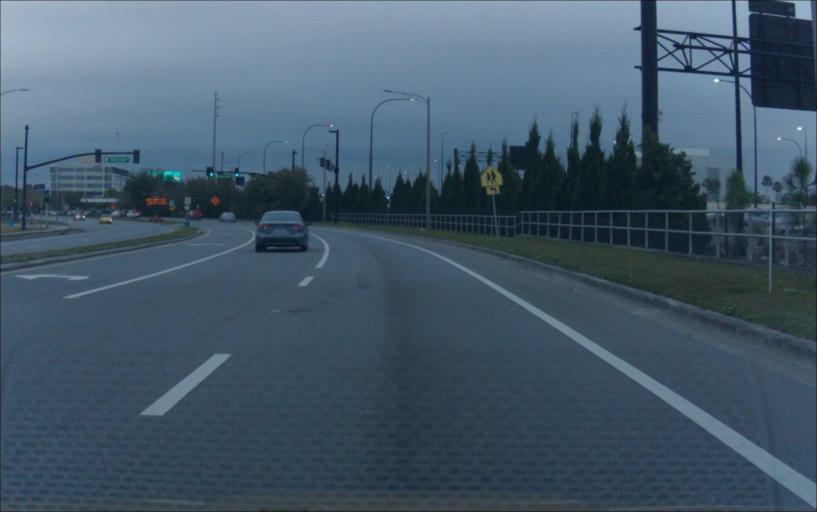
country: US
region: Florida
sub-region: Orange County
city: Oak Ridge
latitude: 28.4925
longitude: -81.4366
